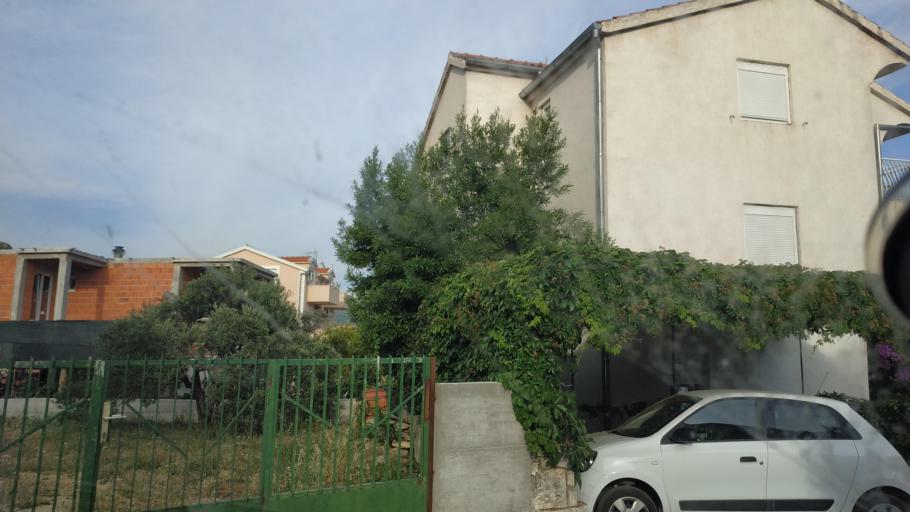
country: HR
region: Sibensko-Kniniska
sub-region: Grad Sibenik
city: Brodarica
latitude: 43.6367
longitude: 15.9615
